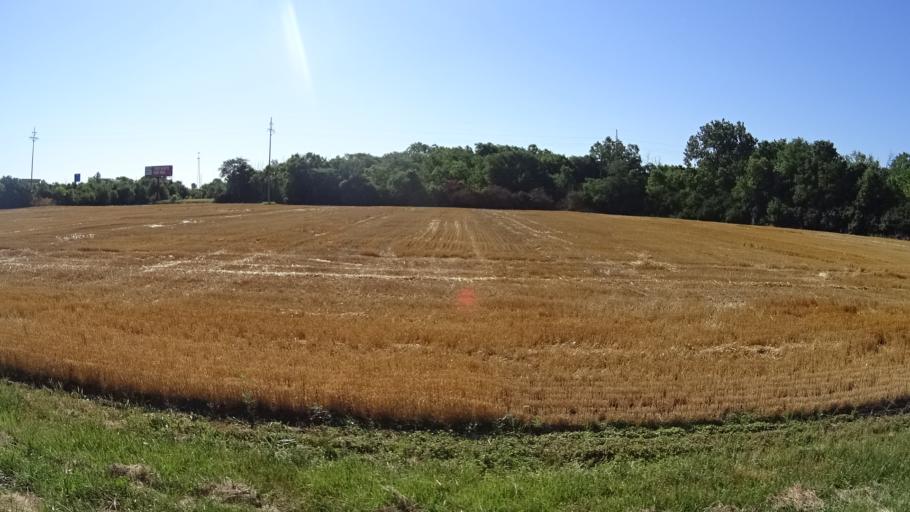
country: US
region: Ohio
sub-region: Erie County
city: Sandusky
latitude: 41.4076
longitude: -82.7450
